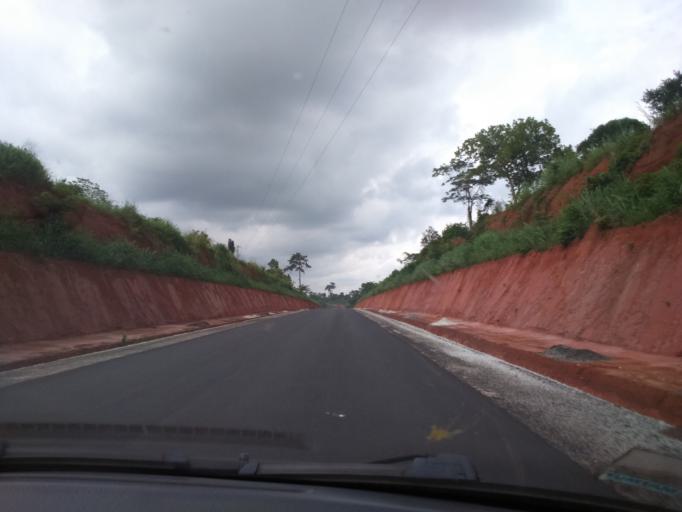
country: CI
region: Lagunes
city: Akoupe
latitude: 6.5035
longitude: -3.8230
